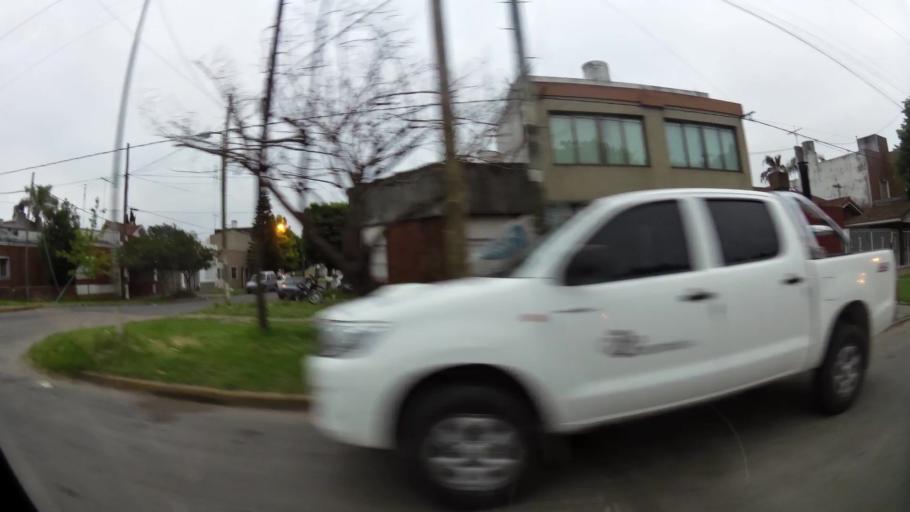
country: AR
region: Buenos Aires
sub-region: Partido de La Plata
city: La Plata
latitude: -34.9030
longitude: -57.9725
